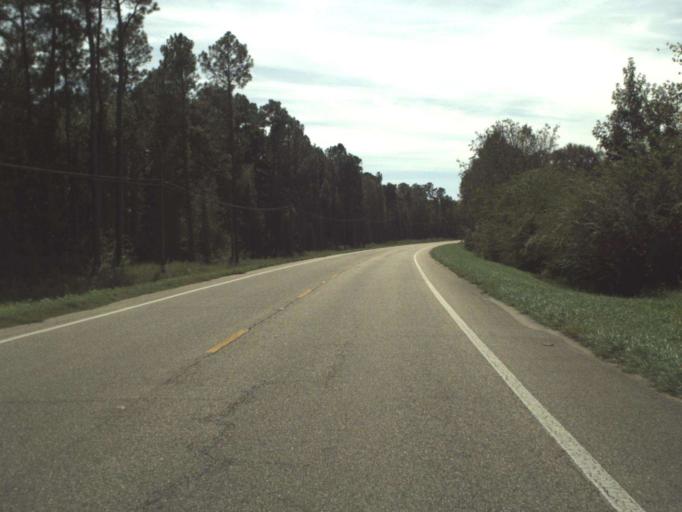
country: US
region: Florida
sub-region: Washington County
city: Chipley
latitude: 30.8501
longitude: -85.5291
